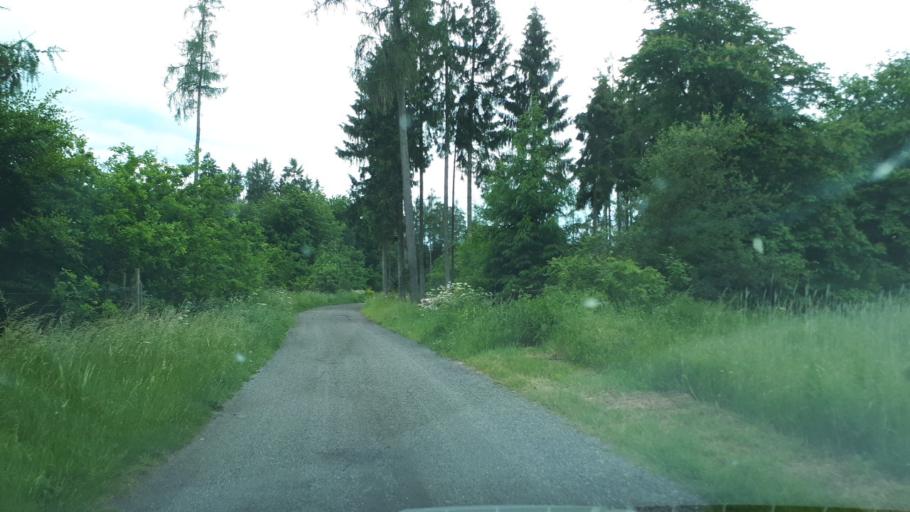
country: DE
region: Rheinland-Pfalz
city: Greimersburg
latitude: 50.2052
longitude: 7.1167
